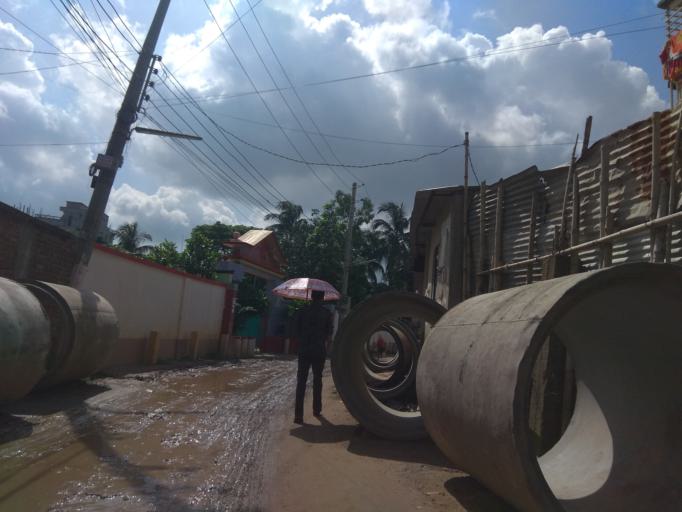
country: BD
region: Dhaka
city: Tungi
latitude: 23.8166
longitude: 90.3859
